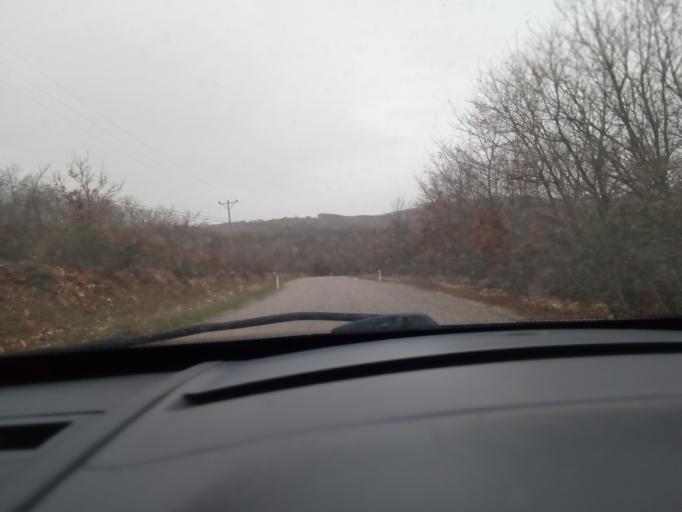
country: TR
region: Balikesir
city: Omerkoy
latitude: 39.9217
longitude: 28.0631
